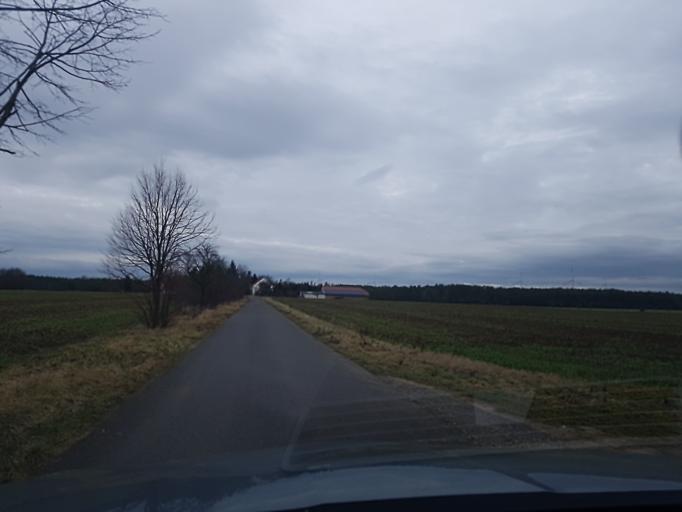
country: DE
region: Brandenburg
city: Schilda
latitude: 51.6296
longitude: 13.3547
